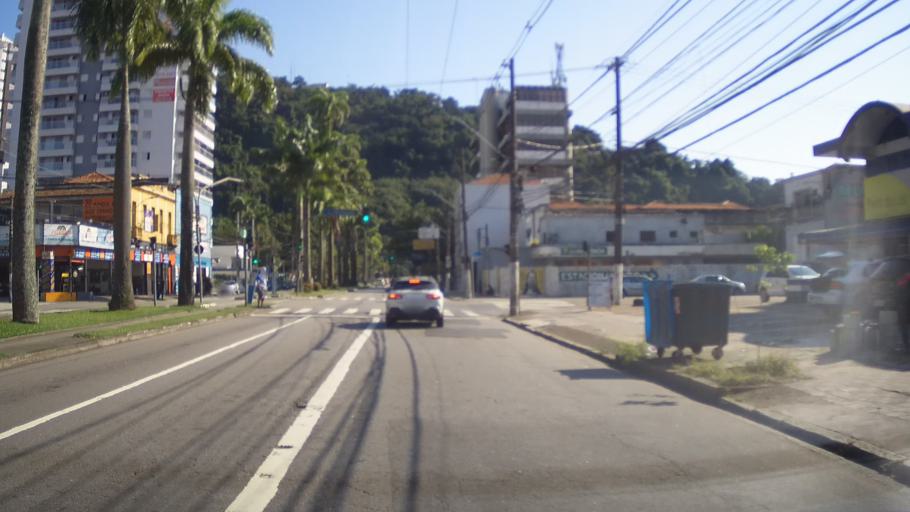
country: BR
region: Sao Paulo
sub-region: Santos
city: Santos
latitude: -23.9456
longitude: -46.3301
